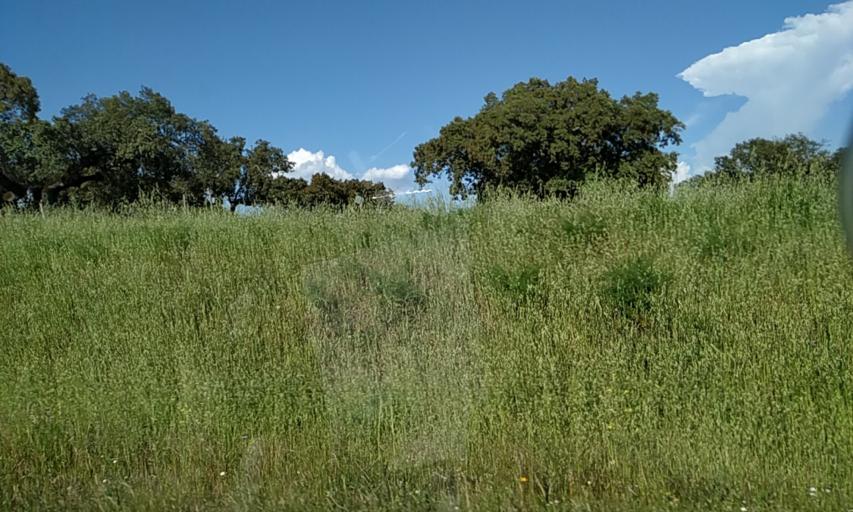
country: PT
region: Portalegre
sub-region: Portalegre
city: Urra
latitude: 39.0848
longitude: -7.4380
